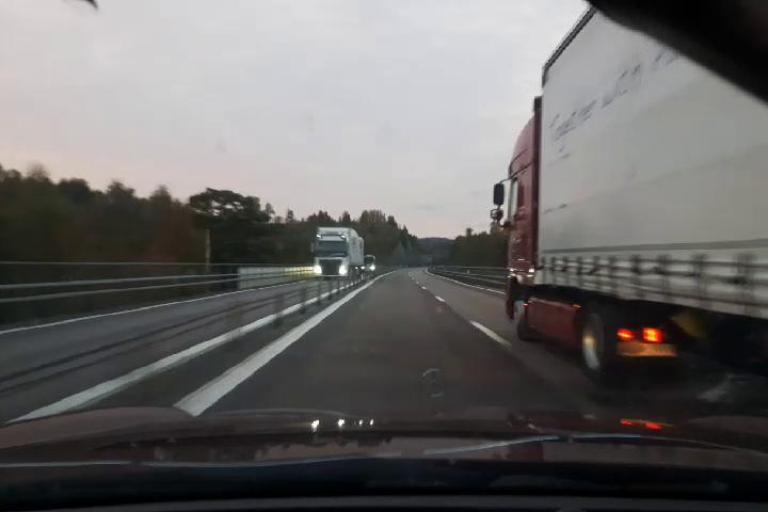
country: SE
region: Vaesternorrland
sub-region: Haernoesands Kommun
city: Haernoesand
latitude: 62.8310
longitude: 17.9679
